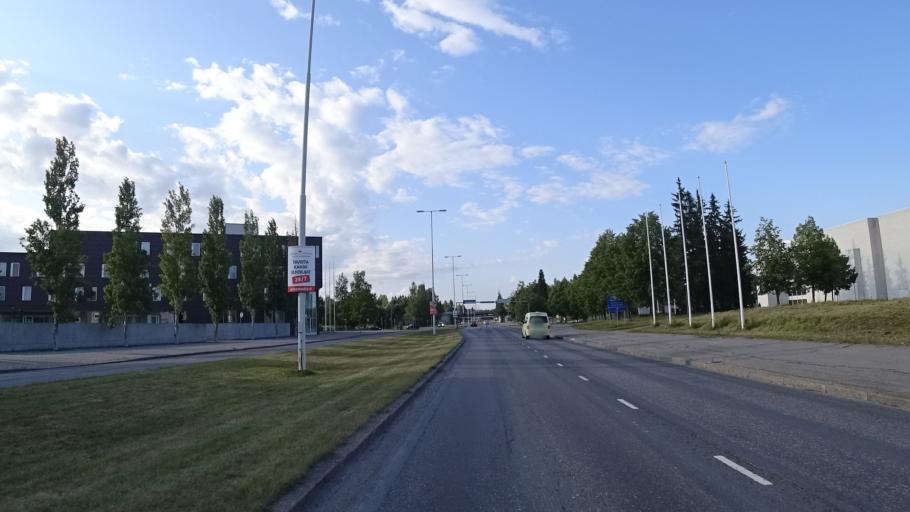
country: FI
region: South Karelia
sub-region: Imatra
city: Imatra
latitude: 61.1907
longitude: 28.7770
